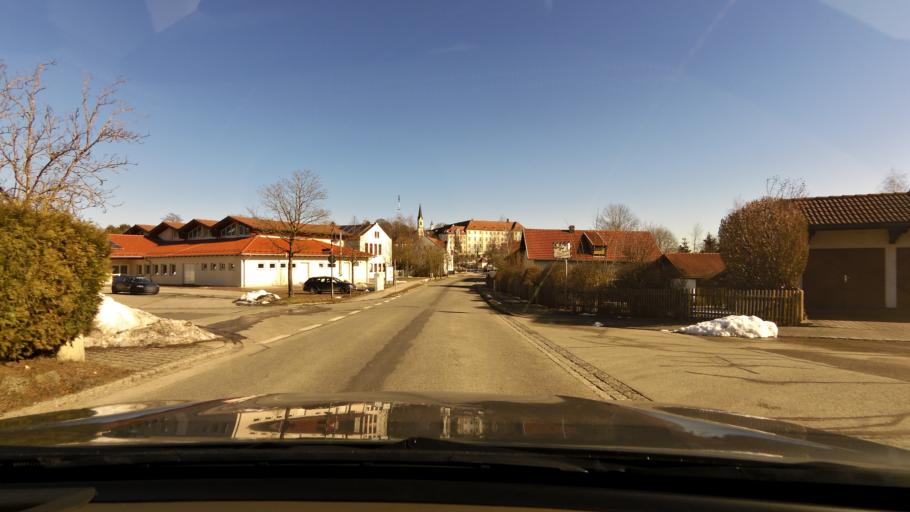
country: DE
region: Bavaria
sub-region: Upper Bavaria
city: Zangberg
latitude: 48.2737
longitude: 12.4214
